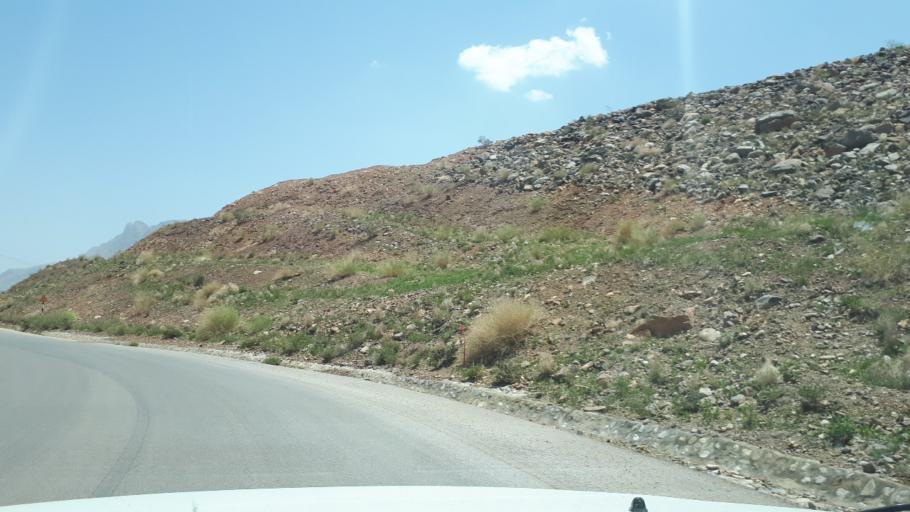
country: OM
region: Muhafazat ad Dakhiliyah
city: Bahla'
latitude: 23.1911
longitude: 57.1371
